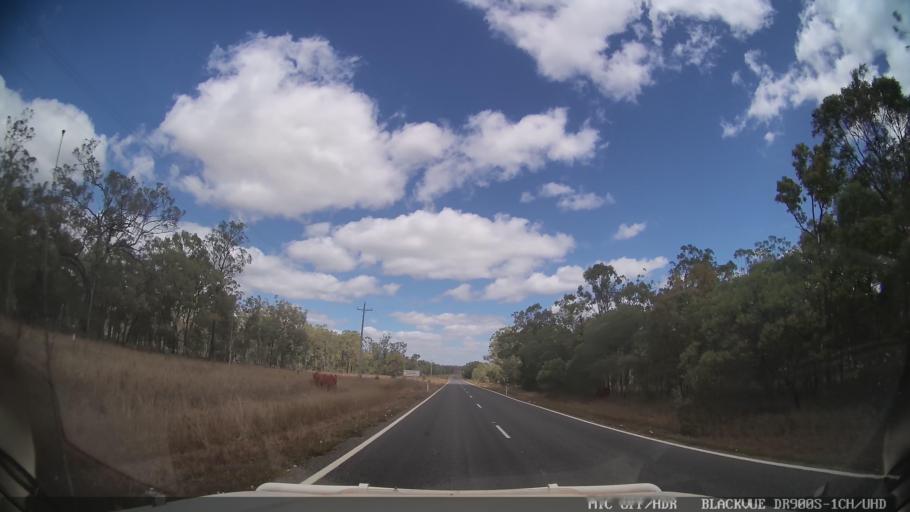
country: AU
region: Queensland
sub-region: Tablelands
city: Ravenshoe
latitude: -18.0265
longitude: 144.8701
